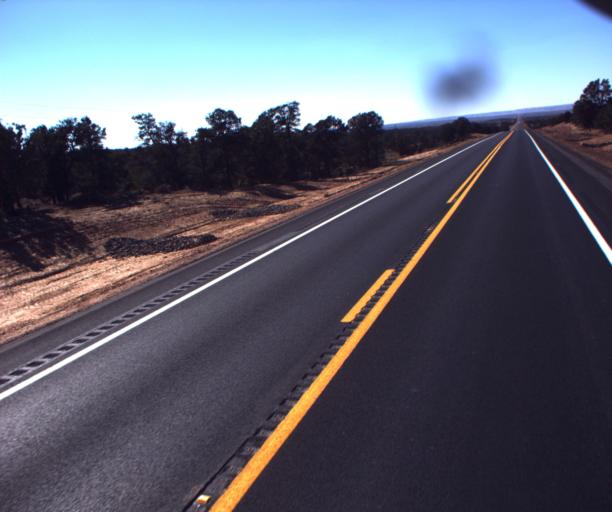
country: US
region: Arizona
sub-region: Apache County
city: Ganado
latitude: 35.7193
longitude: -109.3749
